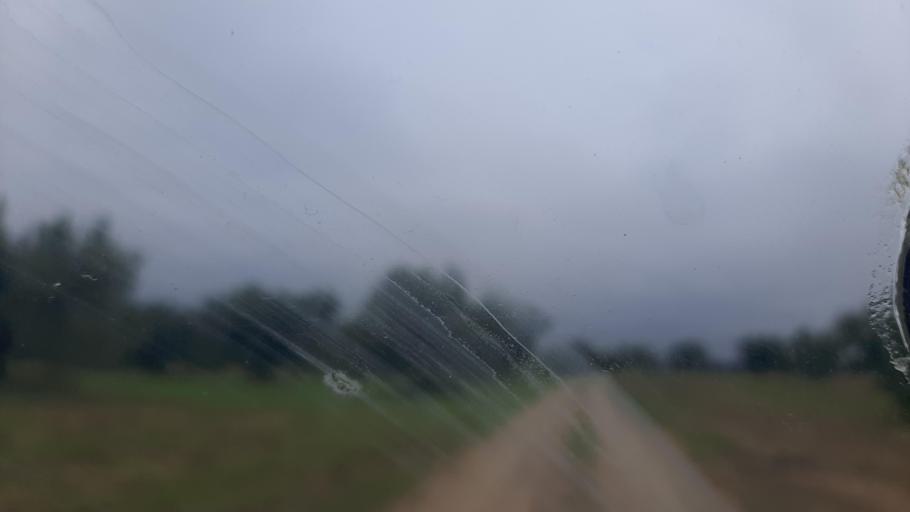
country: TN
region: Tunis
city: La Sebala du Mornag
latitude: 36.5786
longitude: 10.2905
